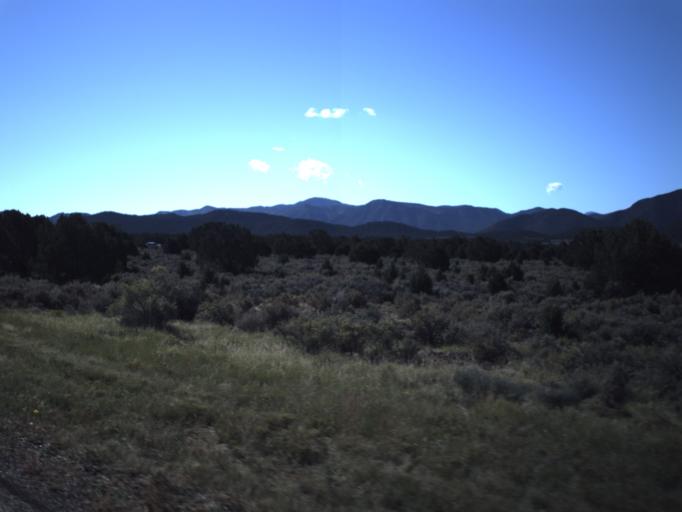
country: US
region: Utah
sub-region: Washington County
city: Enterprise
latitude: 37.6351
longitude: -113.4316
